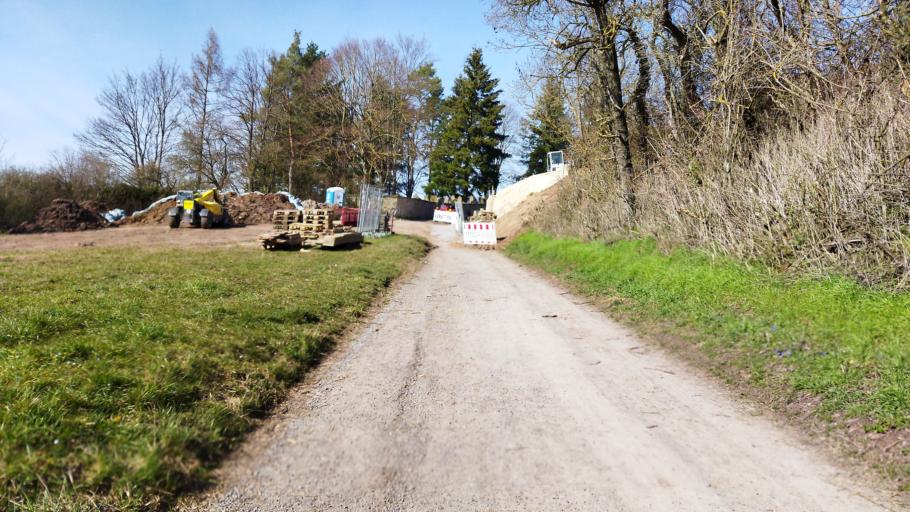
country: DE
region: Baden-Wuerttemberg
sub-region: Regierungsbezirk Stuttgart
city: Eppingen
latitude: 49.1279
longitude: 8.9049
